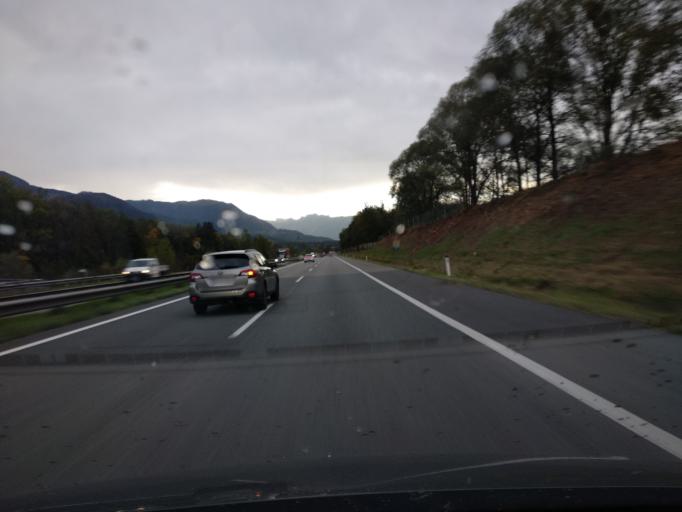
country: AT
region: Vorarlberg
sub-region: Politischer Bezirk Feldkirch
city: Schlins
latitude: 47.1975
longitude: 9.6928
